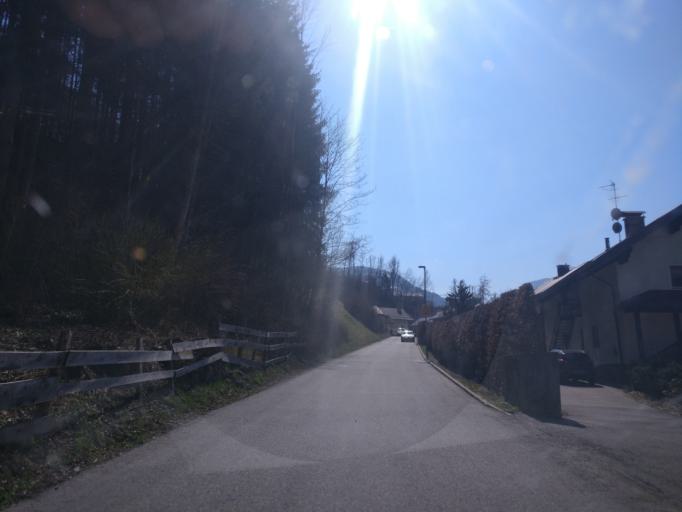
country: AT
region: Salzburg
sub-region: Politischer Bezirk Sankt Johann im Pongau
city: Sankt Johann im Pongau
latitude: 47.3545
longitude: 13.2070
